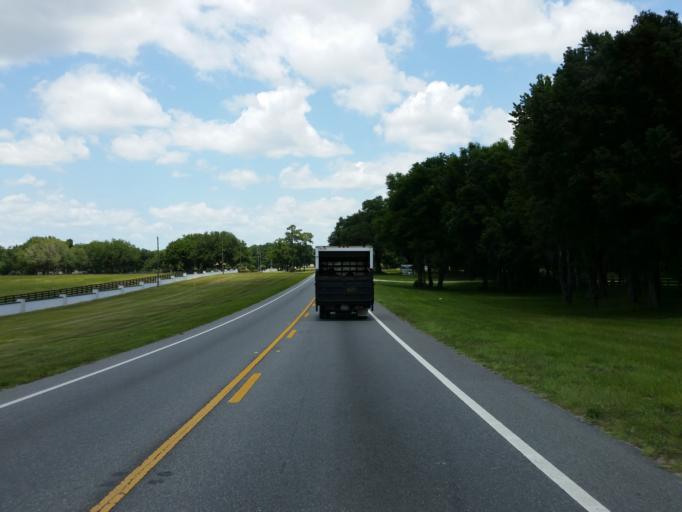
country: US
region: Florida
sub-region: Marion County
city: Belleview
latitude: 28.9951
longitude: -82.0413
